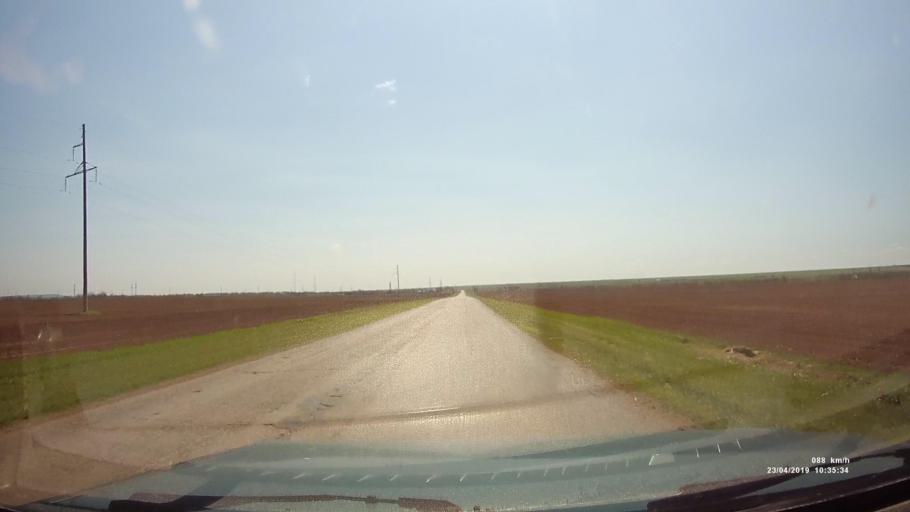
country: RU
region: Kalmykiya
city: Yashalta
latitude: 46.5527
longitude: 42.6257
